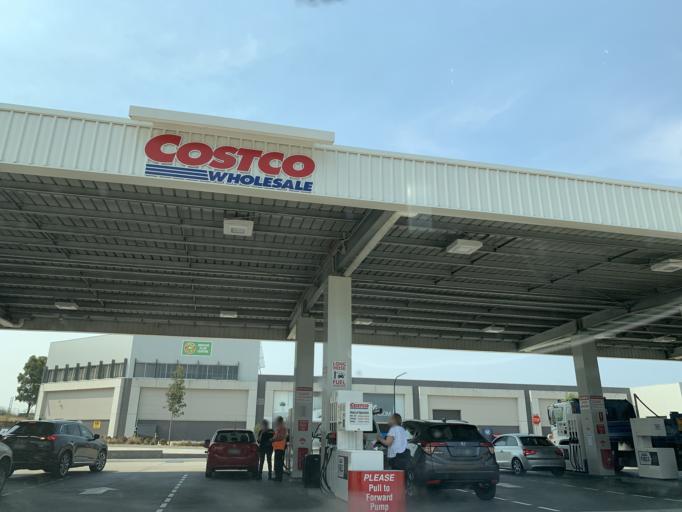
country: AU
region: New South Wales
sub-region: Blacktown
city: Hassall Grove
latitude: -33.7214
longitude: 150.8399
